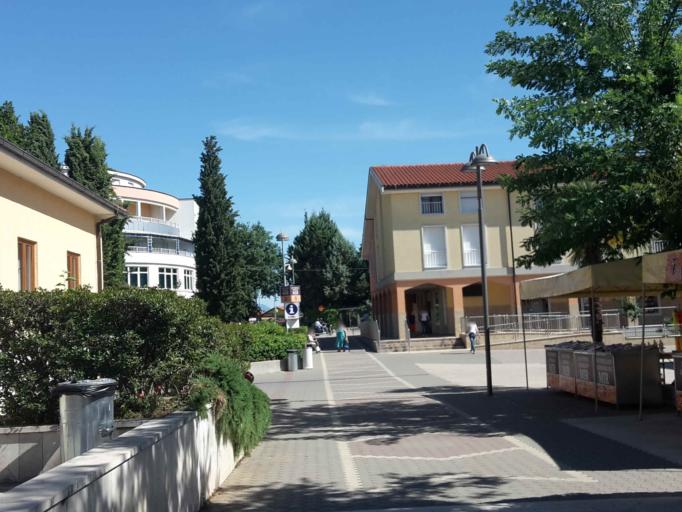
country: BA
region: Federation of Bosnia and Herzegovina
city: Citluk
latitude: 43.1906
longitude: 17.6780
